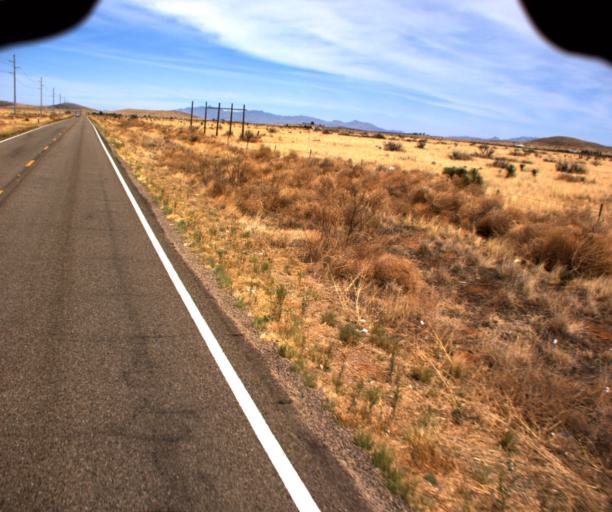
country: US
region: Arizona
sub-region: Cochise County
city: Tombstone
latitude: 31.8575
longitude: -109.6951
